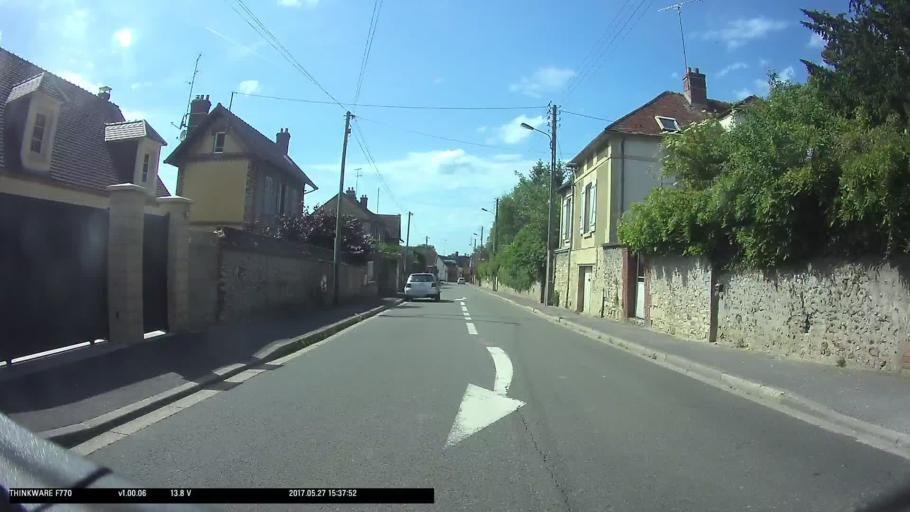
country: FR
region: Picardie
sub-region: Departement de l'Oise
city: Chaumont-en-Vexin
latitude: 49.2630
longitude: 1.8755
